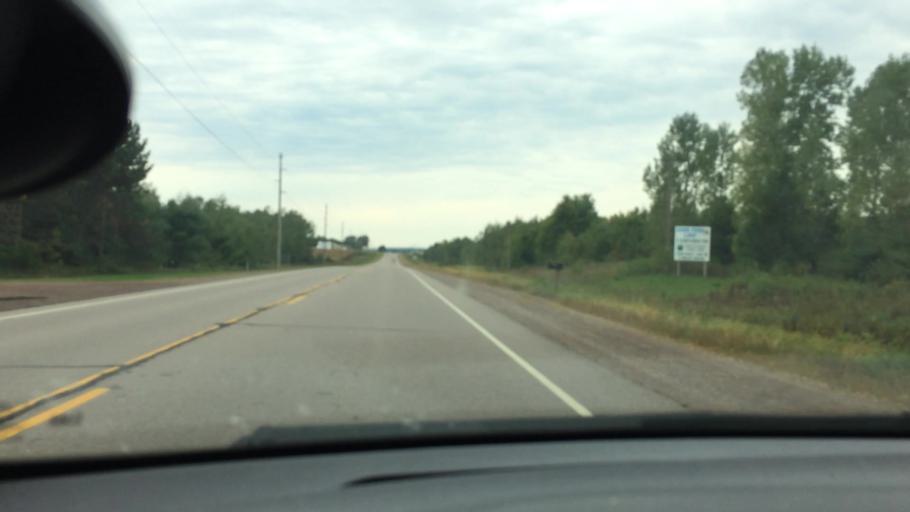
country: US
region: Wisconsin
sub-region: Eau Claire County
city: Augusta
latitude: 44.5963
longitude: -90.9226
